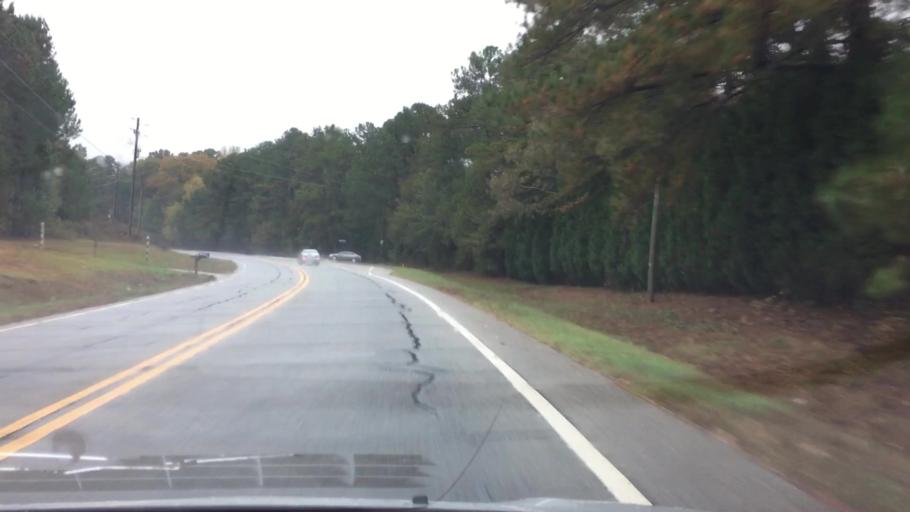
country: US
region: Georgia
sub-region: Henry County
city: Stockbridge
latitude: 33.5621
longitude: -84.1374
